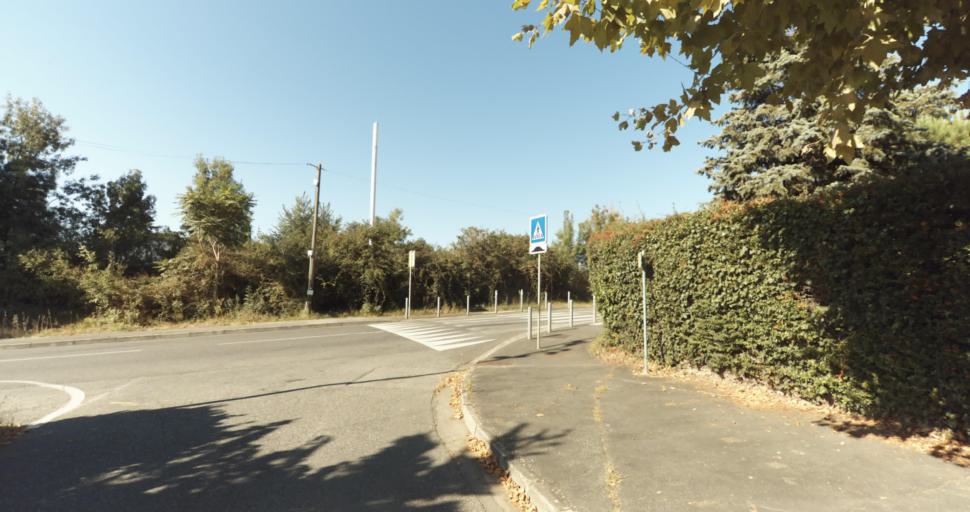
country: FR
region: Midi-Pyrenees
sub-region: Departement de la Haute-Garonne
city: Saint-Genies-Bellevue
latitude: 43.6766
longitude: 1.4780
